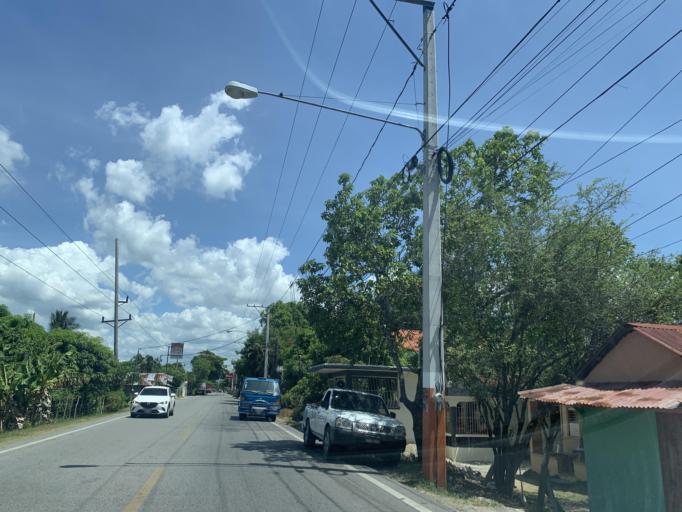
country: DO
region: Puerto Plata
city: Cabarete
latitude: 19.7112
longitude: -70.3850
